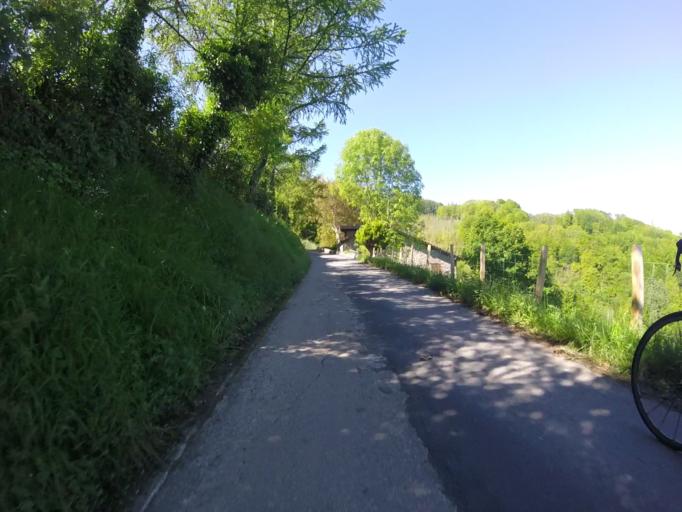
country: ES
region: Basque Country
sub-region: Provincia de Guipuzcoa
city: Beizama
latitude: 43.1683
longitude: -2.2095
